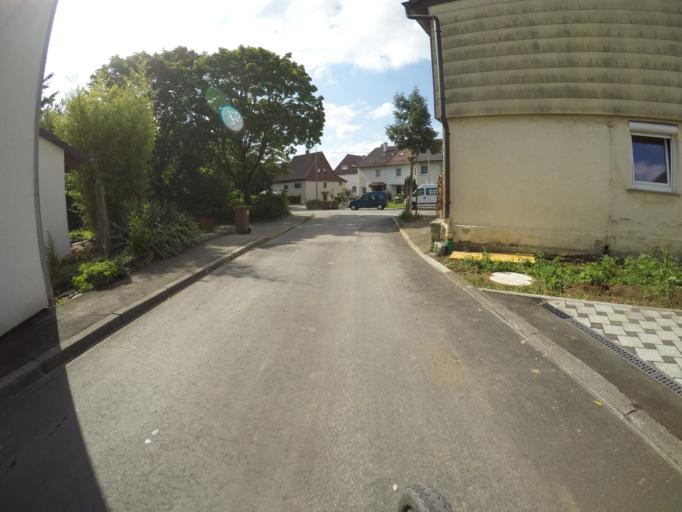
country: DE
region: Baden-Wuerttemberg
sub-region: Regierungsbezirk Stuttgart
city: Unterensingen
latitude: 48.6434
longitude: 9.3490
